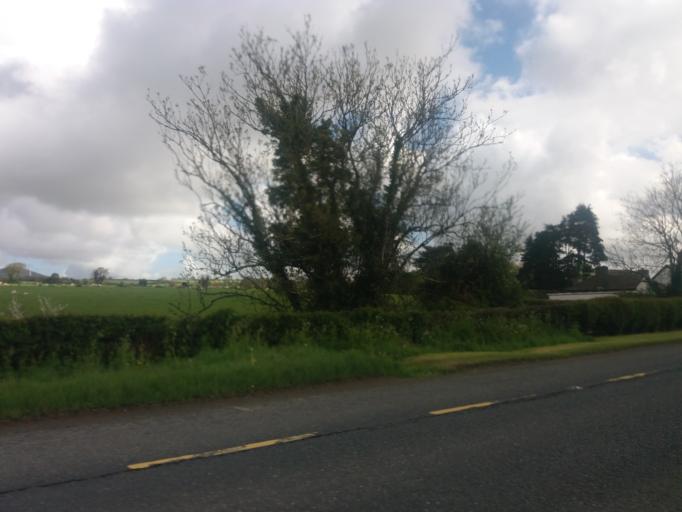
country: IE
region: Leinster
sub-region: Loch Garman
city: Ferns
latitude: 52.6037
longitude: -6.4585
